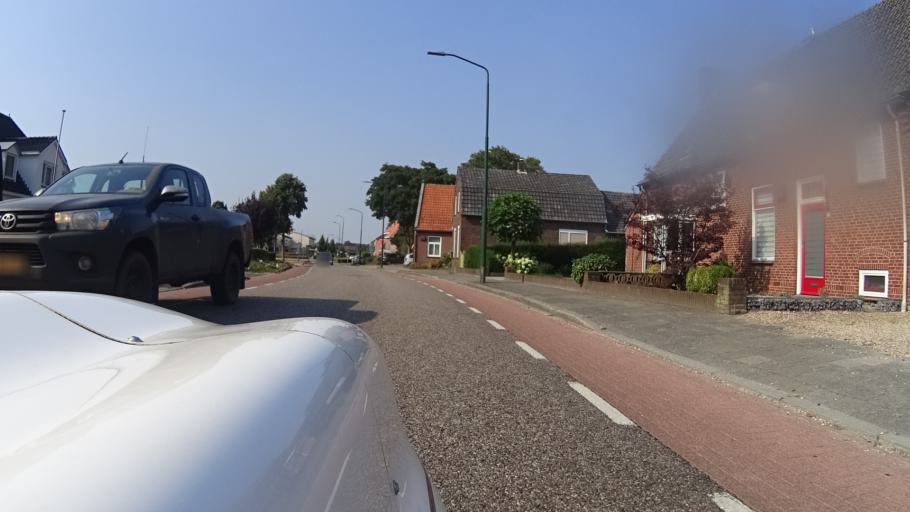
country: NL
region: North Brabant
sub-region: Gemeente Mill en Sint Hubert
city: Wilbertoord
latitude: 51.6854
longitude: 5.7786
